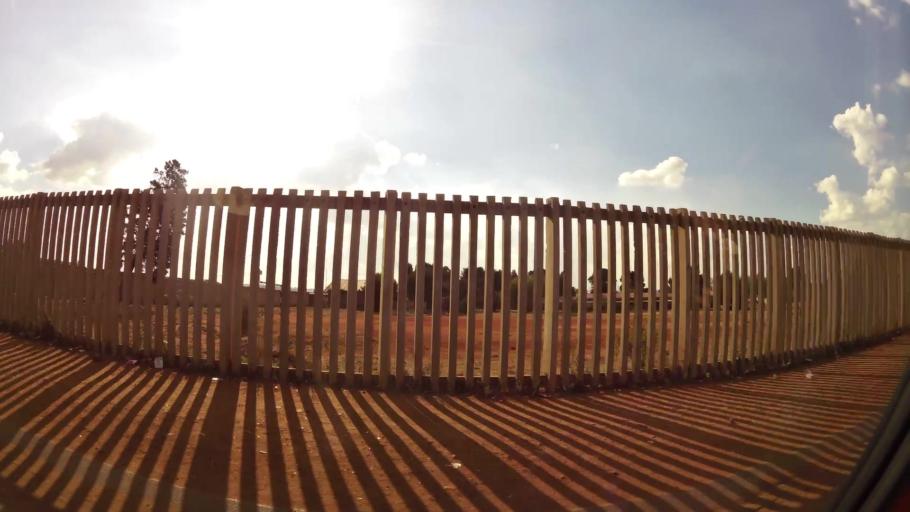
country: ZA
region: Gauteng
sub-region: City of Johannesburg Metropolitan Municipality
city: Soweto
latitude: -26.2242
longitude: 27.8606
